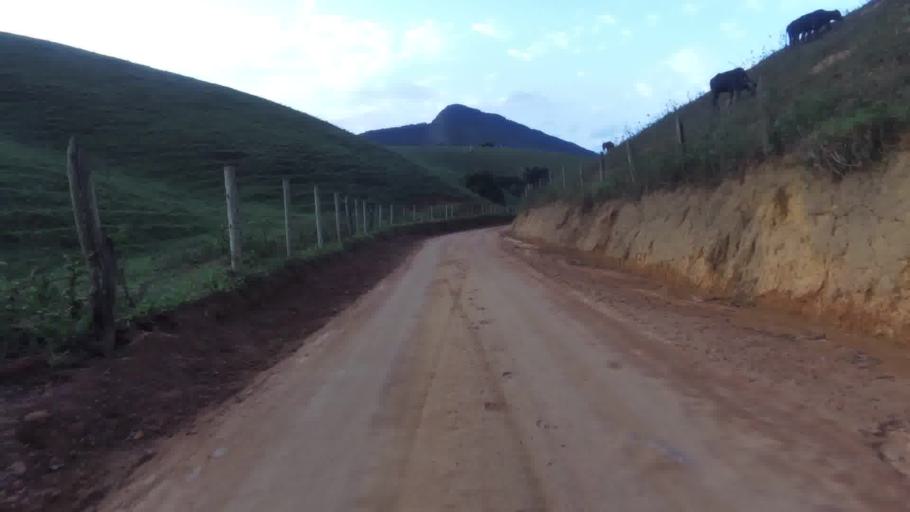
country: BR
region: Espirito Santo
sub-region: Alfredo Chaves
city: Alfredo Chaves
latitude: -20.6925
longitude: -40.6317
